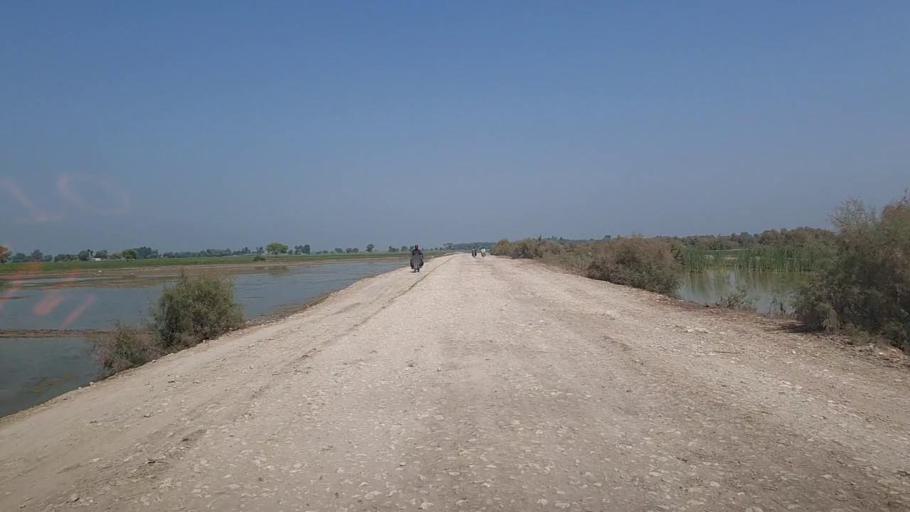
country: PK
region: Sindh
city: Kandhkot
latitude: 28.2984
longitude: 69.2913
